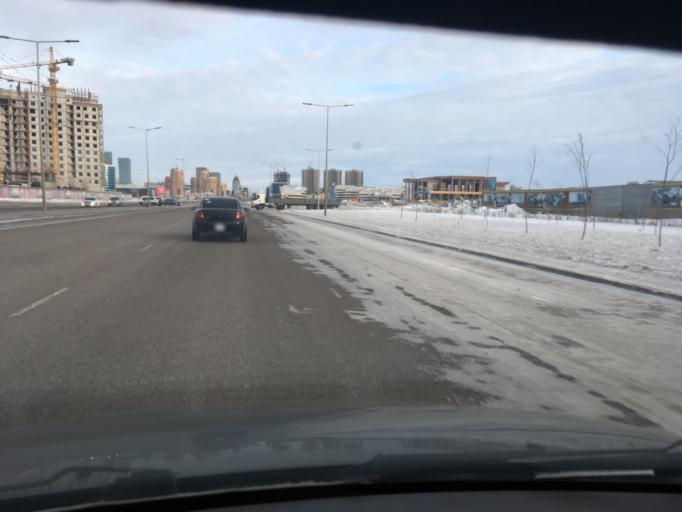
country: KZ
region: Astana Qalasy
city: Astana
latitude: 51.1282
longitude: 71.3942
